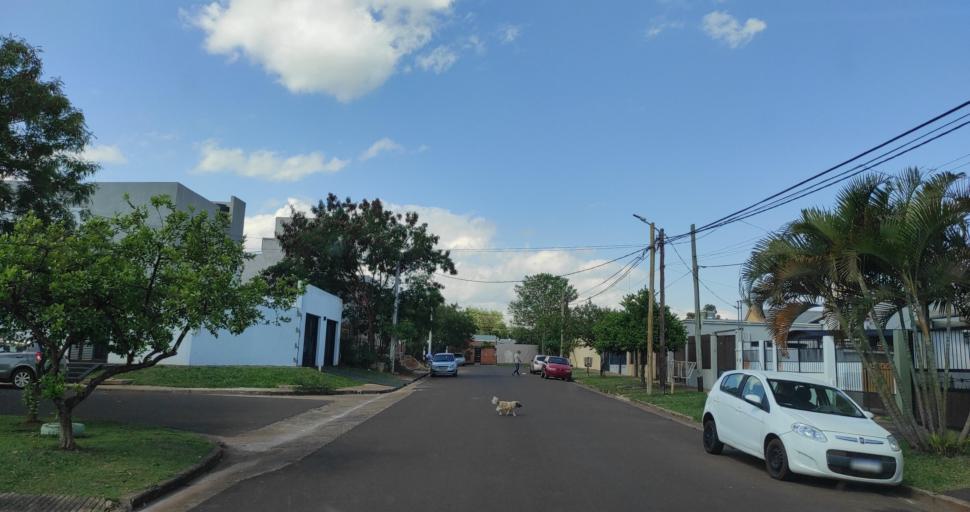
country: AR
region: Misiones
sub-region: Departamento de Capital
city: Posadas
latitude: -27.3837
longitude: -55.9244
